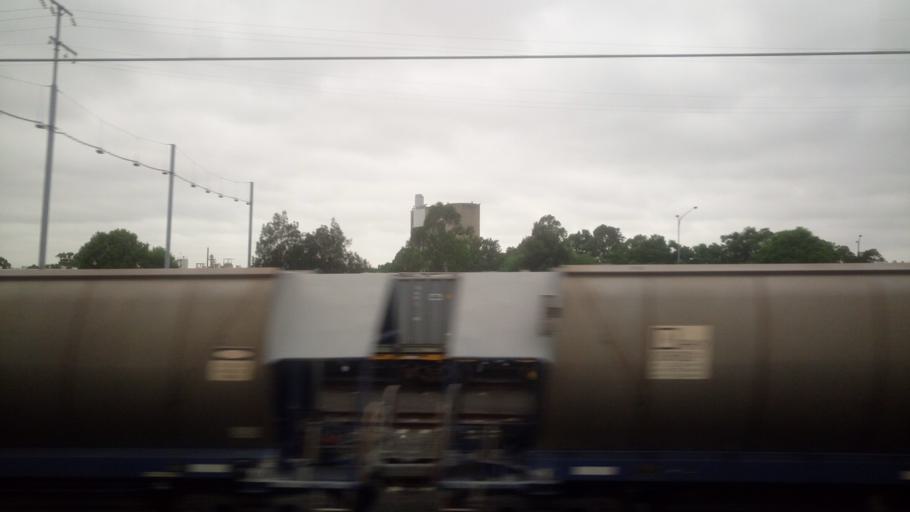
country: AU
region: New South Wales
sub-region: Parramatta
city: Granville
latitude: -33.8408
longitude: 151.0242
